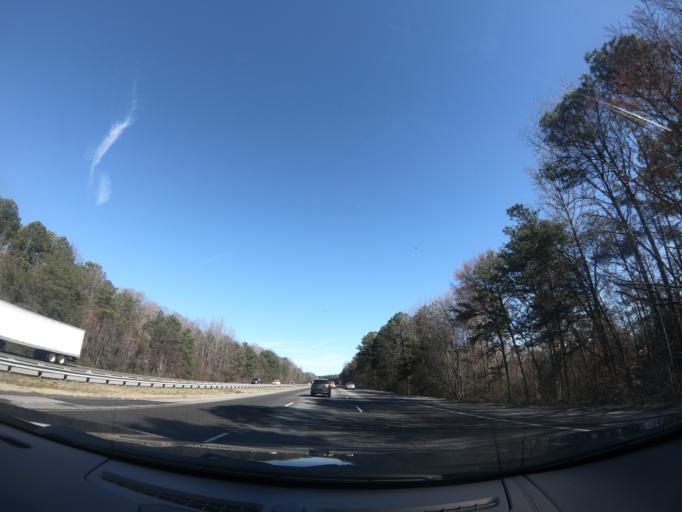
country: US
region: Georgia
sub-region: Whitfield County
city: Dalton
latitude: 34.7301
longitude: -85.0056
